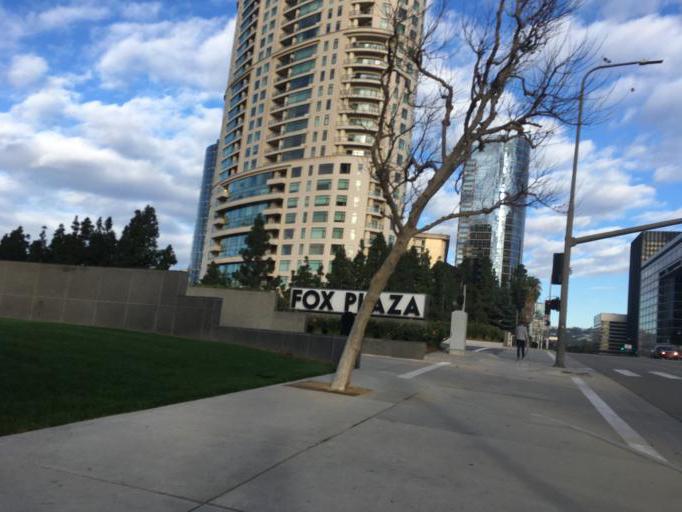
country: US
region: California
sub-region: Los Angeles County
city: Century City
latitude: 34.0558
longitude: -118.4134
